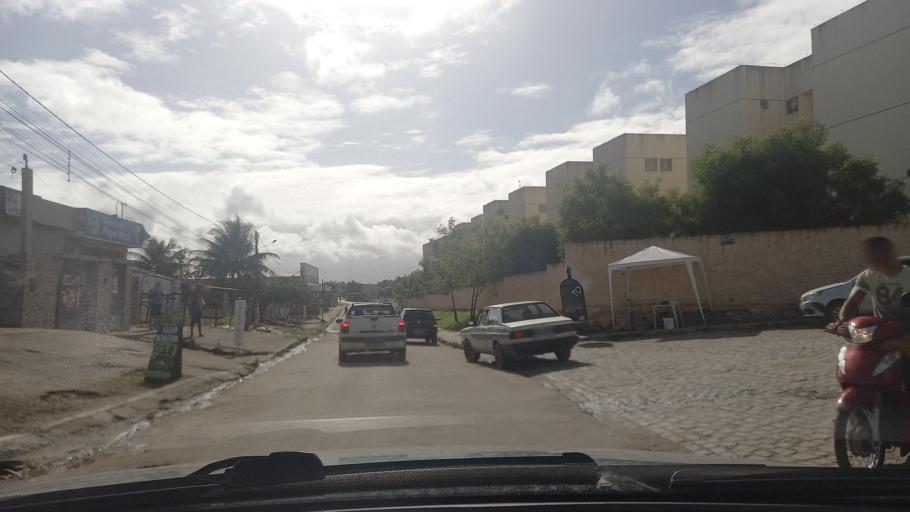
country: BR
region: Pernambuco
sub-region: Vitoria De Santo Antao
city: Vitoria de Santo Antao
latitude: -8.0974
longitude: -35.2773
